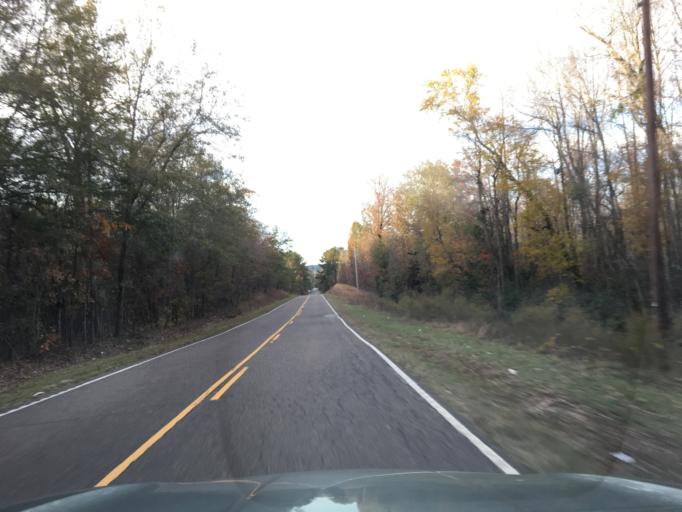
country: US
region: South Carolina
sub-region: Lexington County
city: Red Bank
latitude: 33.7163
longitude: -81.3554
